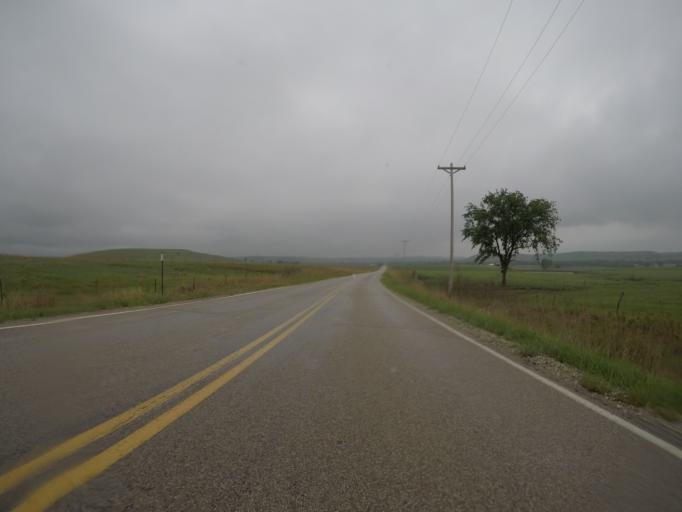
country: US
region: Kansas
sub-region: Pottawatomie County
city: Westmoreland
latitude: 39.4133
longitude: -96.1839
